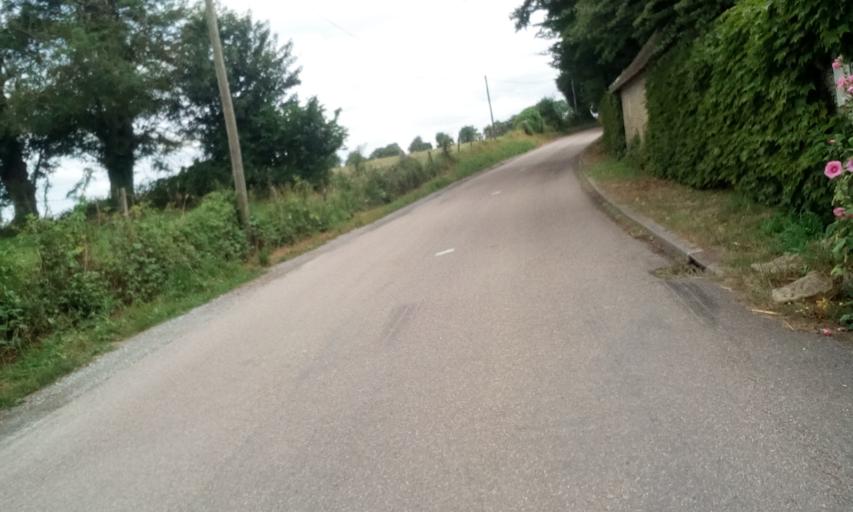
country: FR
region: Lower Normandy
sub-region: Departement du Calvados
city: Bavent
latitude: 49.2125
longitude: -0.1794
